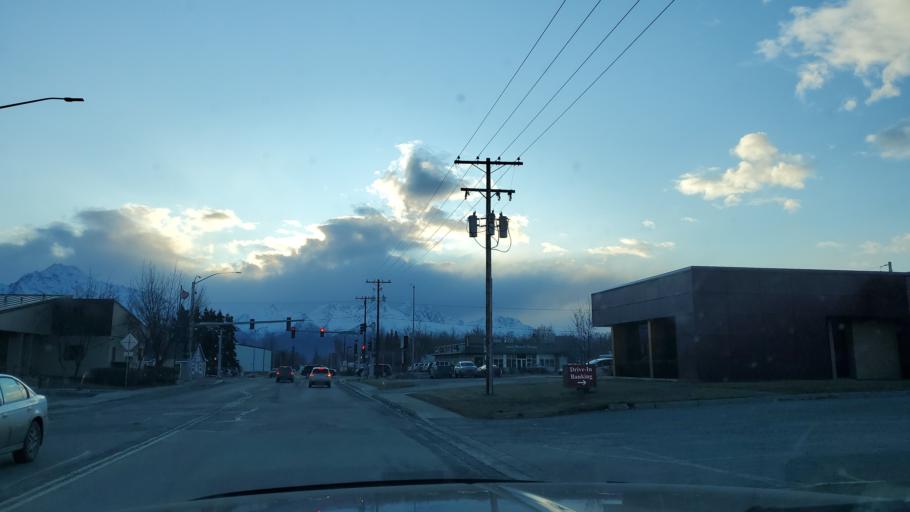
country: US
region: Alaska
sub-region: Matanuska-Susitna Borough
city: Palmer
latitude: 61.6003
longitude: -149.1183
